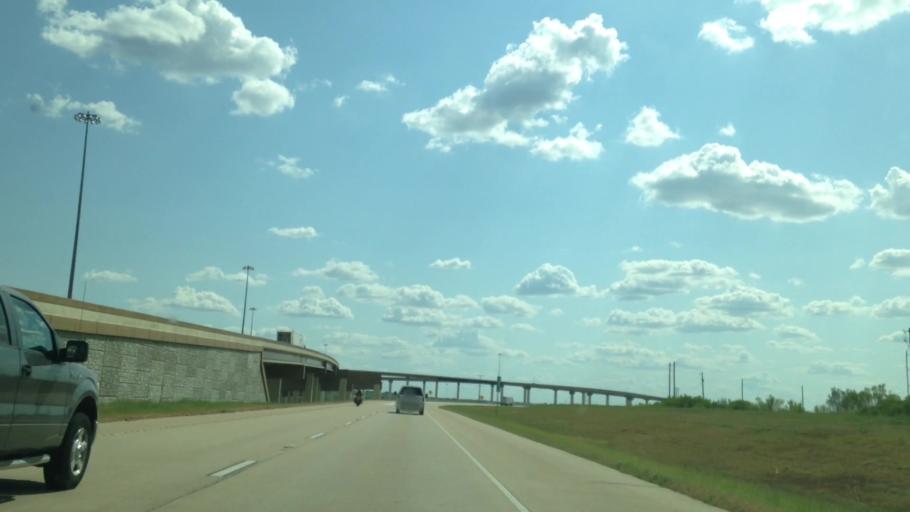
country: US
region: Texas
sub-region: Travis County
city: Onion Creek
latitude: 30.0853
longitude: -97.6876
